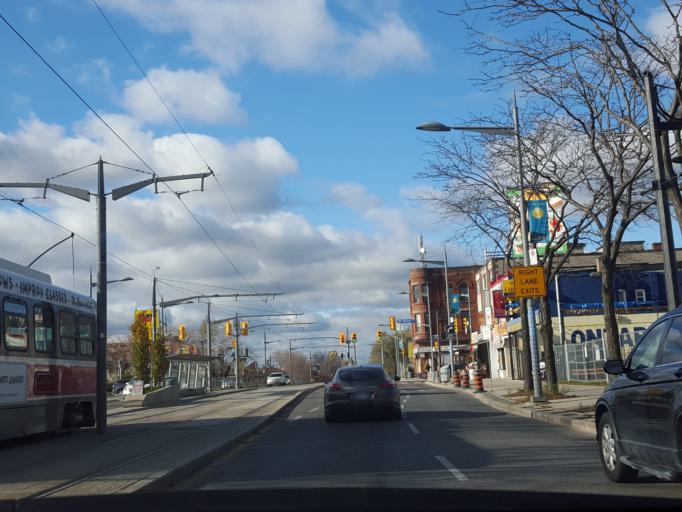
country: CA
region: Ontario
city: Toronto
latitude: 43.6738
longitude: -79.4619
